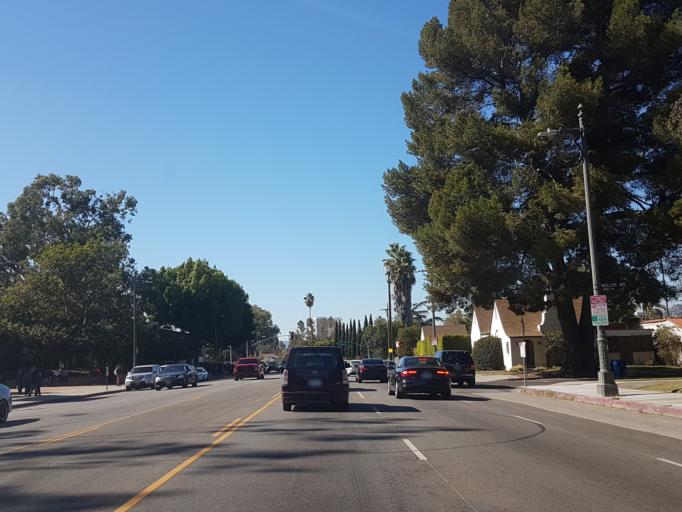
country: US
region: California
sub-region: Los Angeles County
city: Hollywood
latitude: 34.0565
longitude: -118.3321
